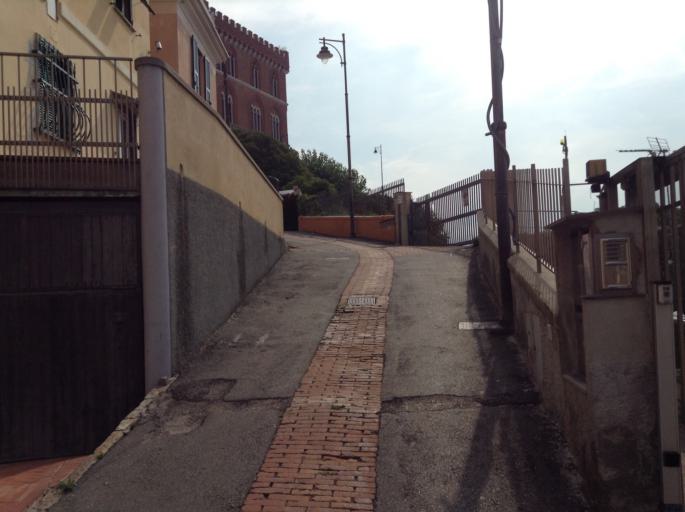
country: IT
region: Liguria
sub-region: Provincia di Genova
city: San Teodoro
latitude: 44.3901
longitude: 8.9756
